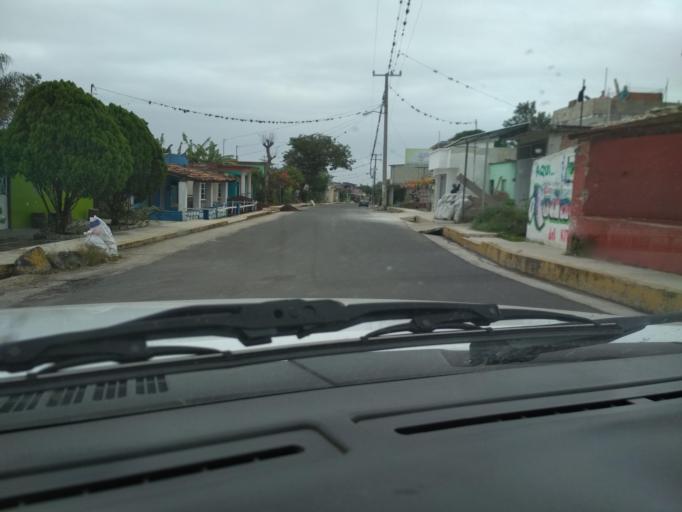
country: MX
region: Veracruz
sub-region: Emiliano Zapata
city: Dos Rios
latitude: 19.5230
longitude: -96.7973
